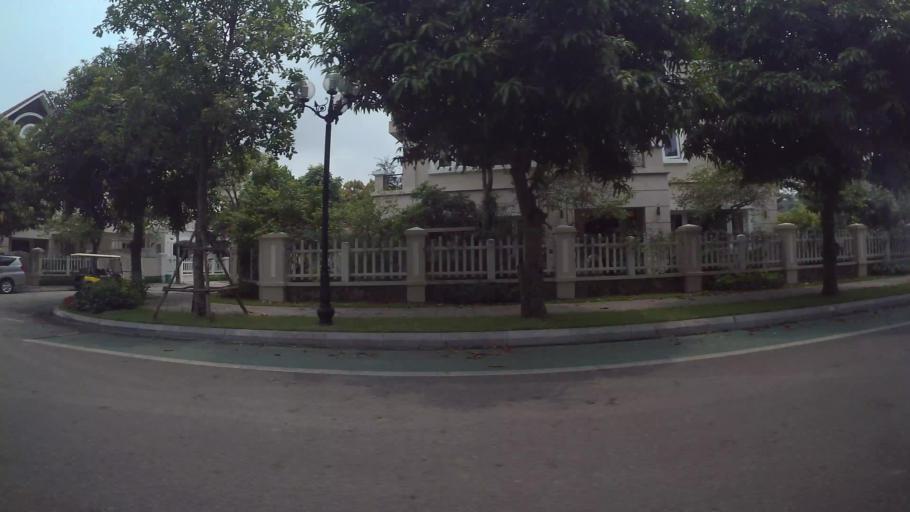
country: VN
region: Ha Noi
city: Trau Quy
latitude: 21.0521
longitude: 105.9142
